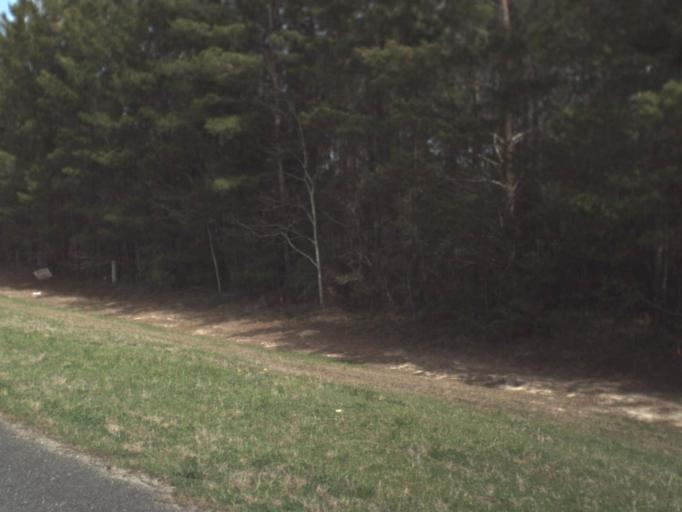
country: US
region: Florida
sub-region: Bay County
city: Youngstown
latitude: 30.5695
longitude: -85.3876
